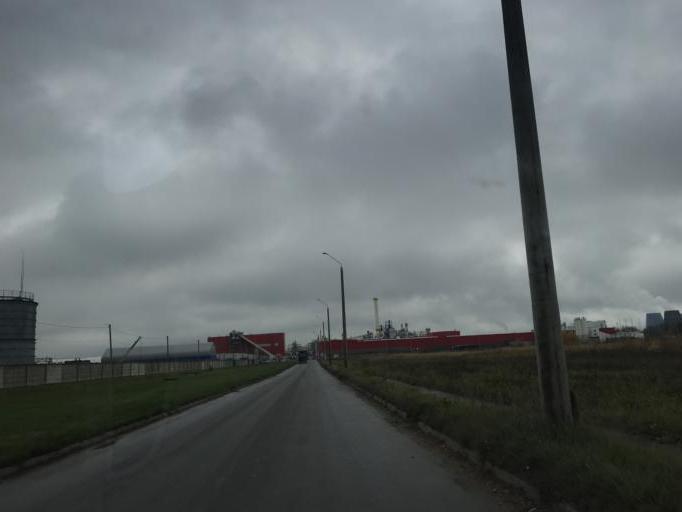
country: BY
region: Mogilev
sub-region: Mahilyowski Rayon
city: Veyno
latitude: 53.8264
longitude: 30.3525
